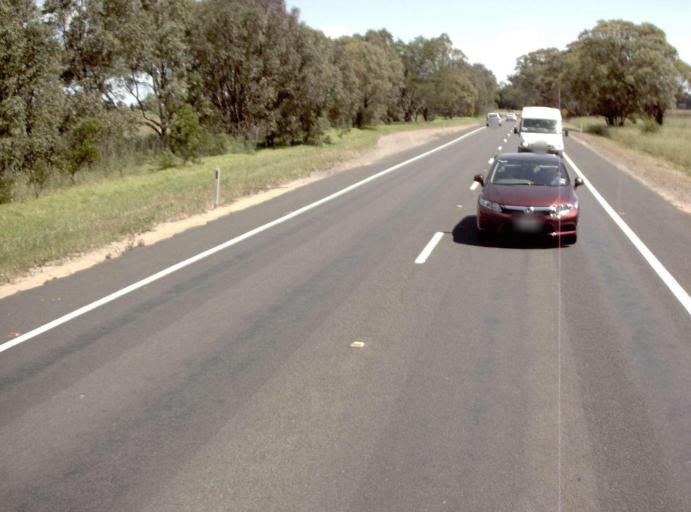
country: AU
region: Victoria
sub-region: Wellington
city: Sale
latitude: -37.9853
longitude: 147.0694
